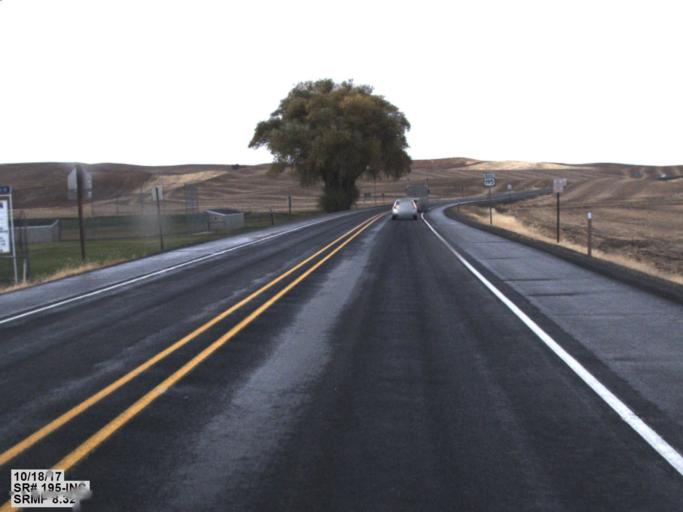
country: US
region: Washington
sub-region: Whitman County
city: Pullman
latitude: 46.5680
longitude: -117.1308
